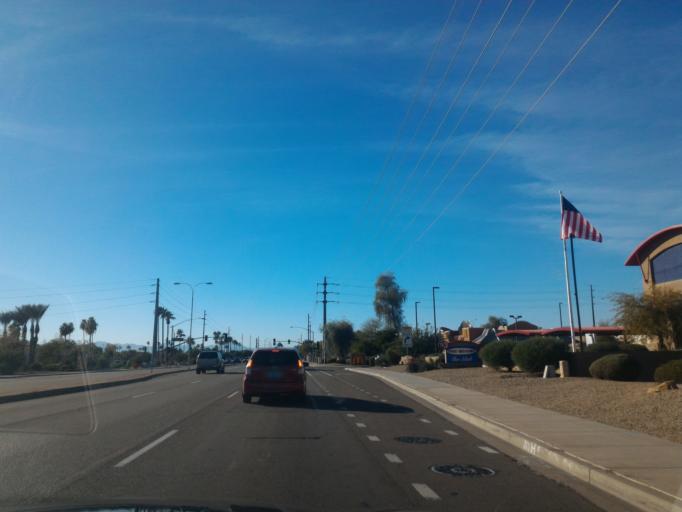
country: US
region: Arizona
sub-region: Maricopa County
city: Guadalupe
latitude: 33.3055
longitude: -111.9440
